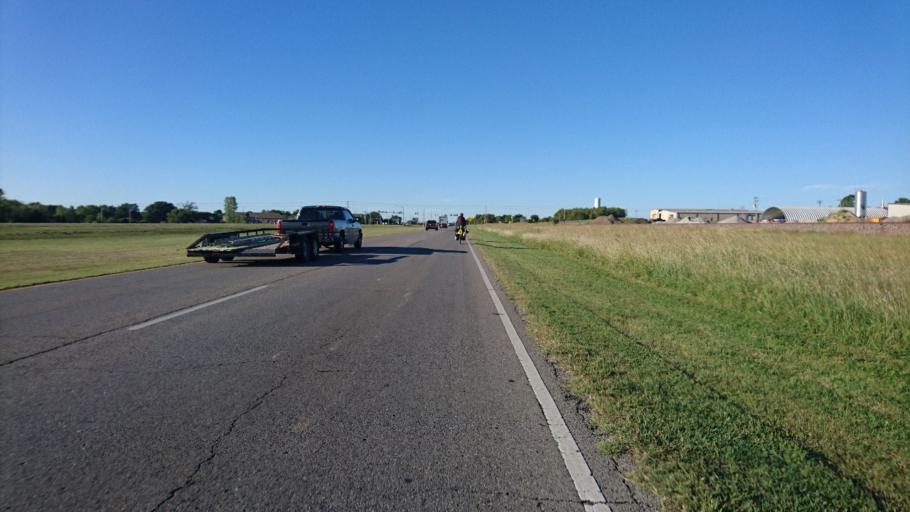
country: US
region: Oklahoma
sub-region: Rogers County
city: Claremore
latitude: 36.2810
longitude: -95.6389
